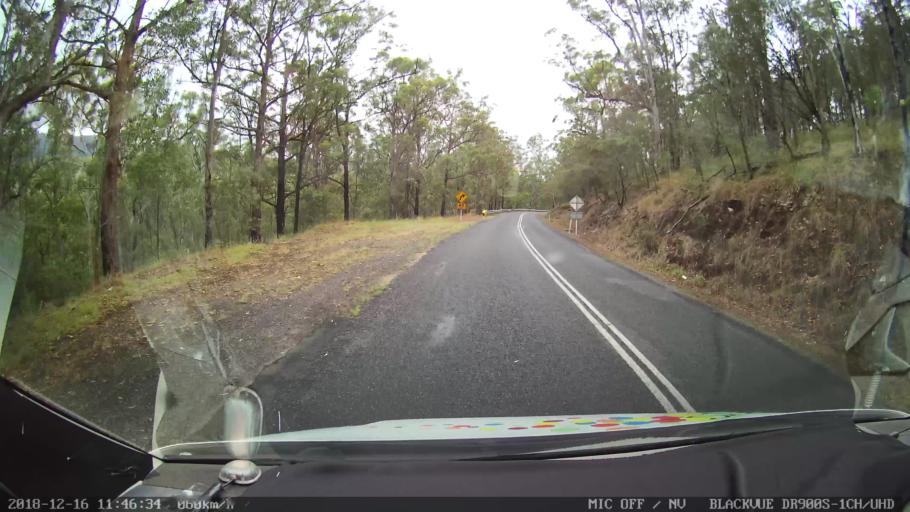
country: AU
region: New South Wales
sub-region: Tenterfield Municipality
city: Carrolls Creek
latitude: -28.9272
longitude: 152.2315
